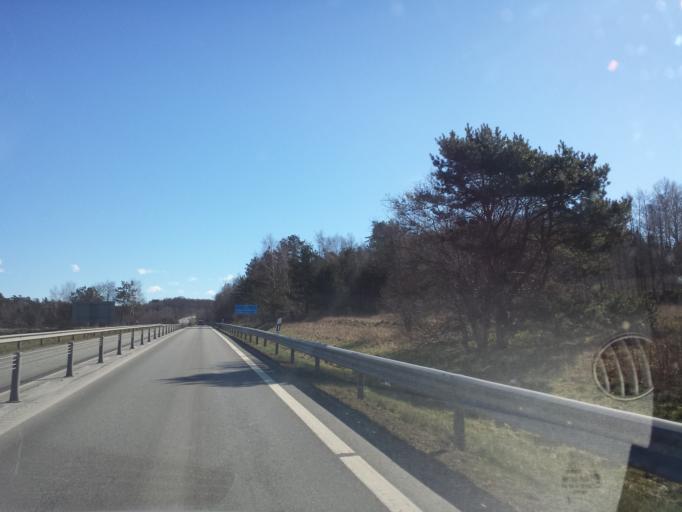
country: SE
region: Skane
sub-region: Sjobo Kommun
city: Sjoebo
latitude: 55.6226
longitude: 13.7098
